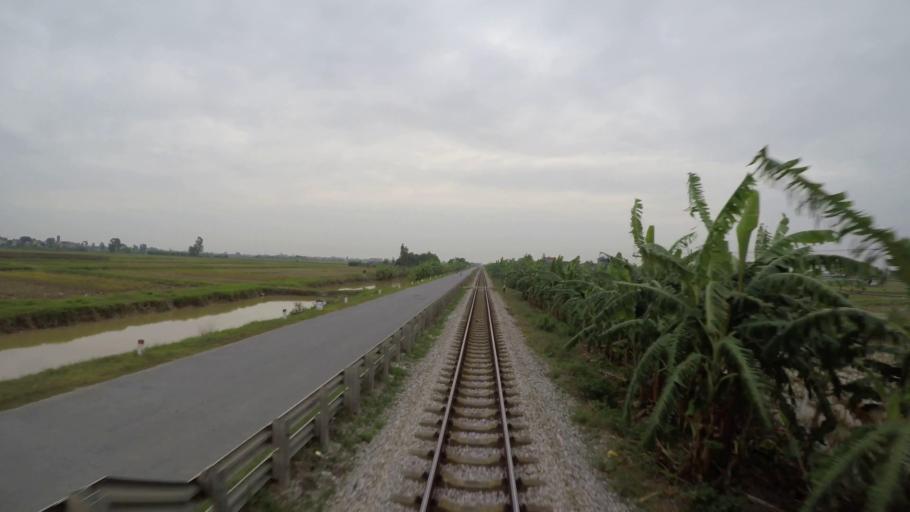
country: VN
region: Hung Yen
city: Ban Yen Nhan
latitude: 20.9812
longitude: 106.0787
